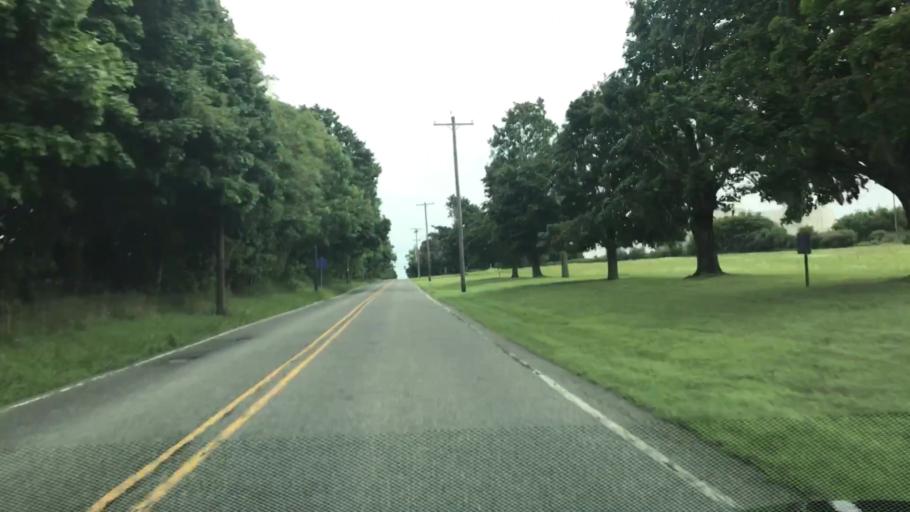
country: US
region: New Jersey
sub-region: Hunterdon County
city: Annandale
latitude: 40.6482
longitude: -74.8610
